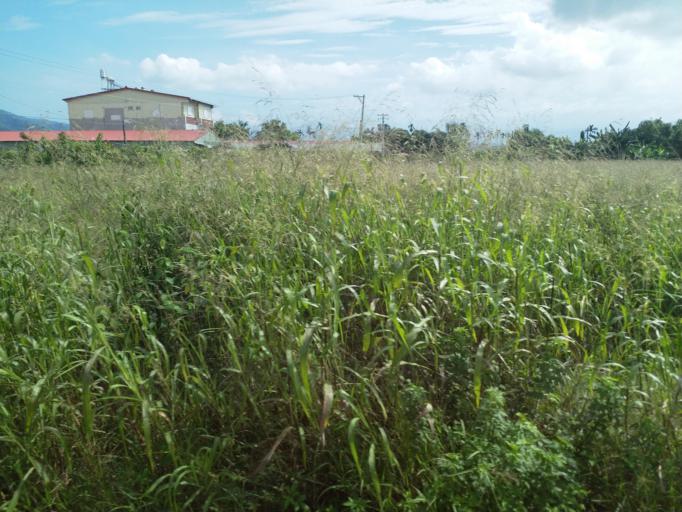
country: TW
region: Taiwan
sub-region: Pingtung
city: Pingtung
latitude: 22.8784
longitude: 120.4967
